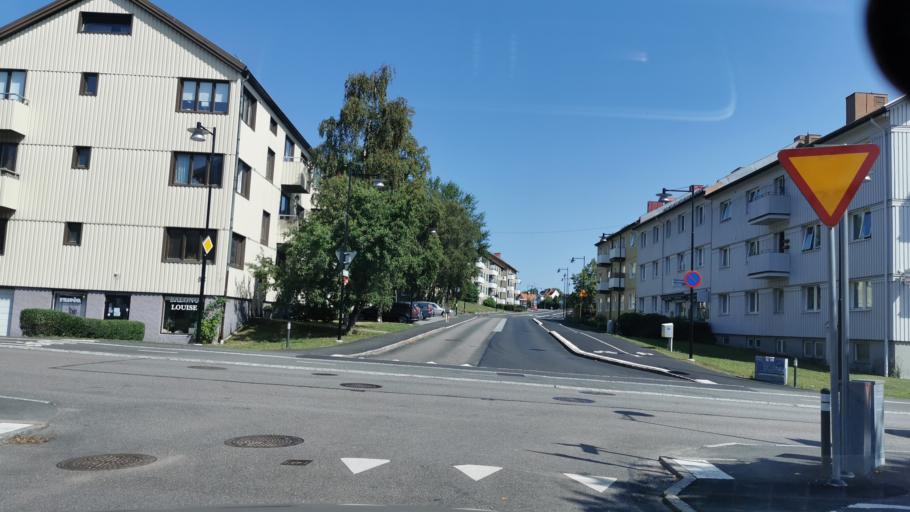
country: SE
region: Vaestra Goetaland
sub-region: Molndal
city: Moelndal
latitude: 57.6759
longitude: 11.9923
